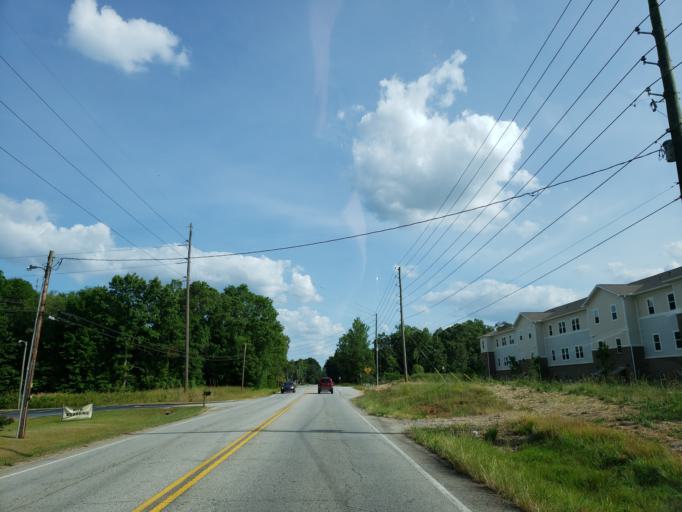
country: US
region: Georgia
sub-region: Carroll County
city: Carrollton
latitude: 33.6082
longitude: -85.0804
